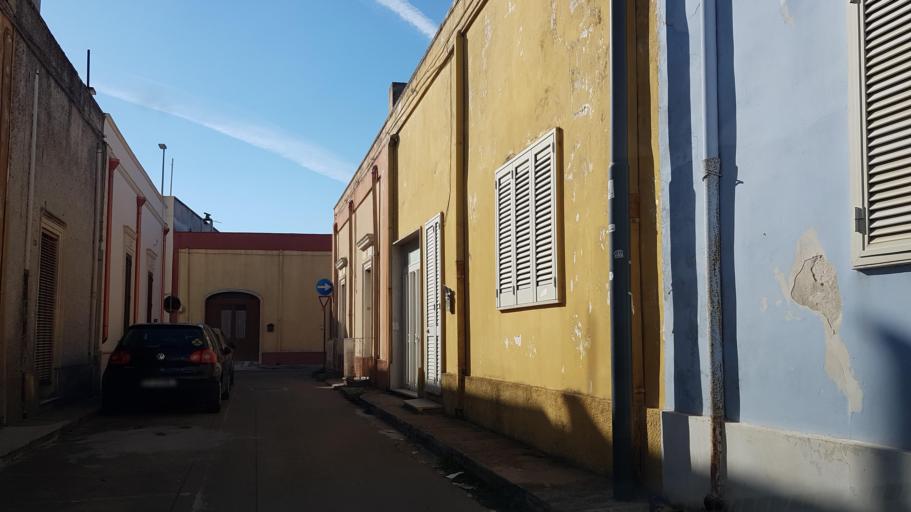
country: IT
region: Apulia
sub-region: Provincia di Lecce
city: Salice Salentino
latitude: 40.3847
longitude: 17.9604
